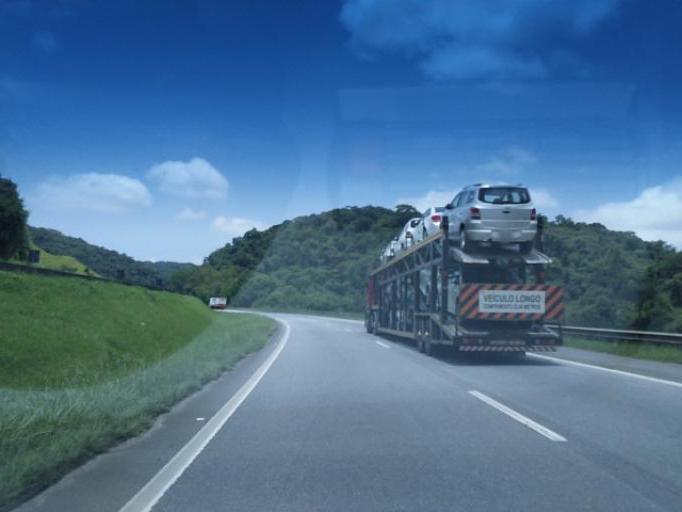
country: BR
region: Sao Paulo
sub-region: Miracatu
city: Miracatu
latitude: -24.1878
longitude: -47.3601
